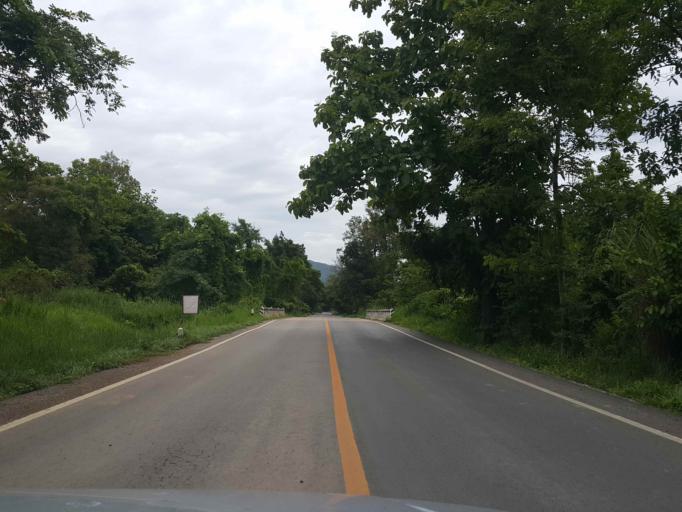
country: TH
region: Lampang
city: Thoen
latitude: 17.5652
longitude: 99.3312
